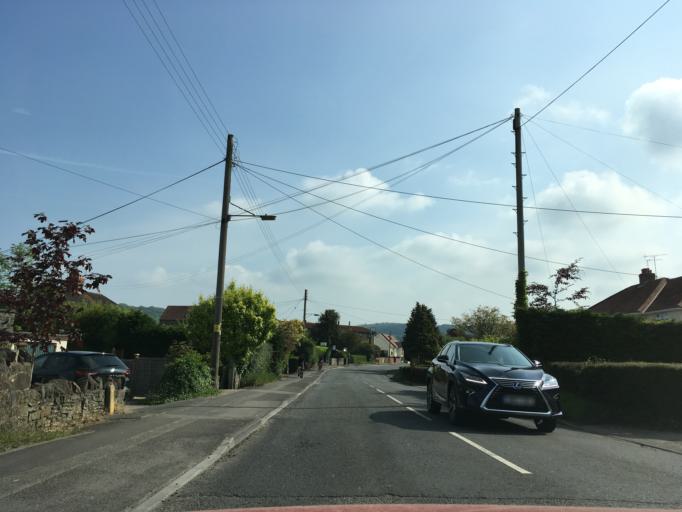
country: GB
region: England
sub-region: North Somerset
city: Nailsea
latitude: 51.4361
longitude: -2.7517
